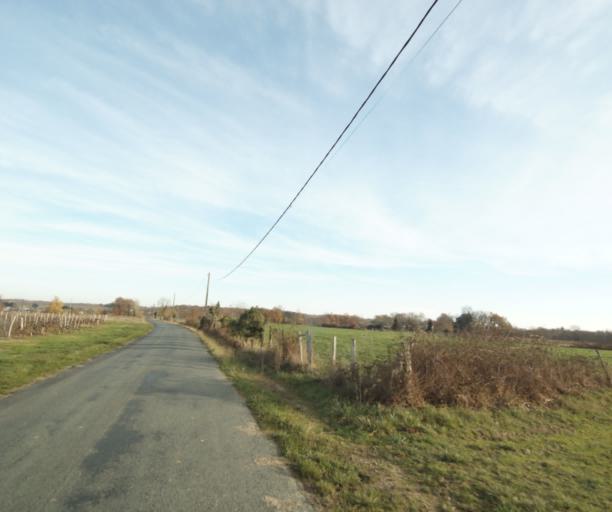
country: FR
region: Poitou-Charentes
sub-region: Departement de la Charente-Maritime
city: Chaniers
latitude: 45.7458
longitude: -0.5499
